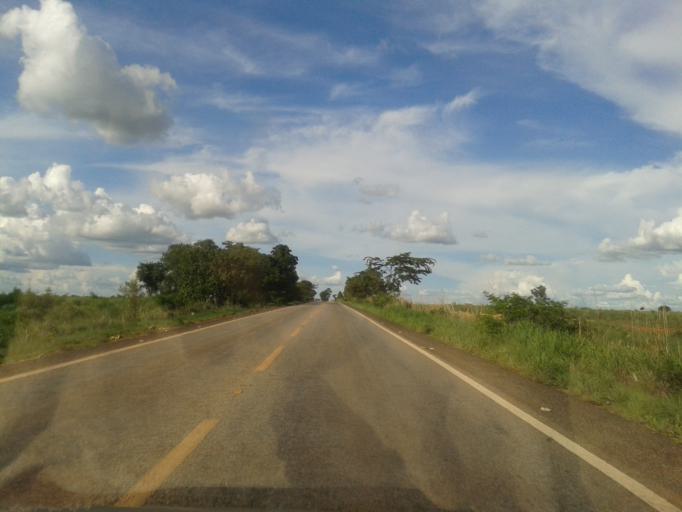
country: BR
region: Goias
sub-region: Mozarlandia
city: Mozarlandia
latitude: -14.5356
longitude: -50.4878
